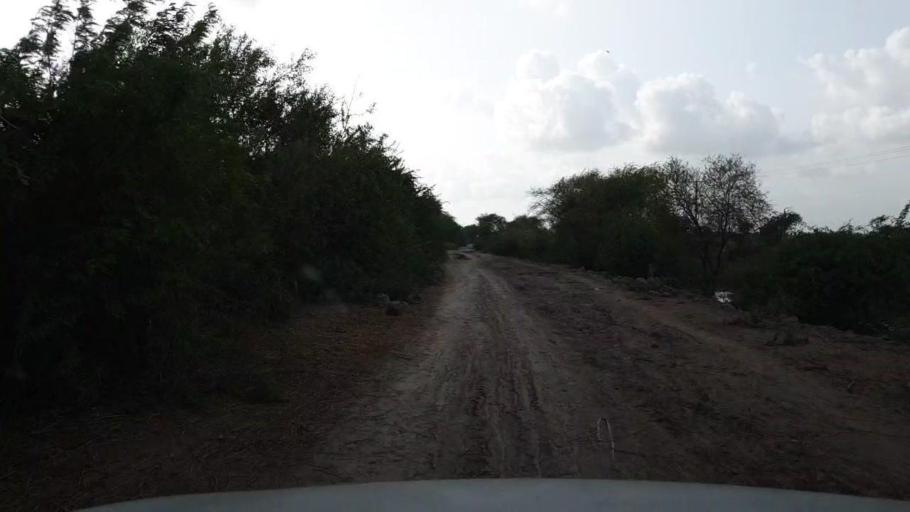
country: PK
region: Sindh
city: Kario
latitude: 24.7602
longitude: 68.6055
